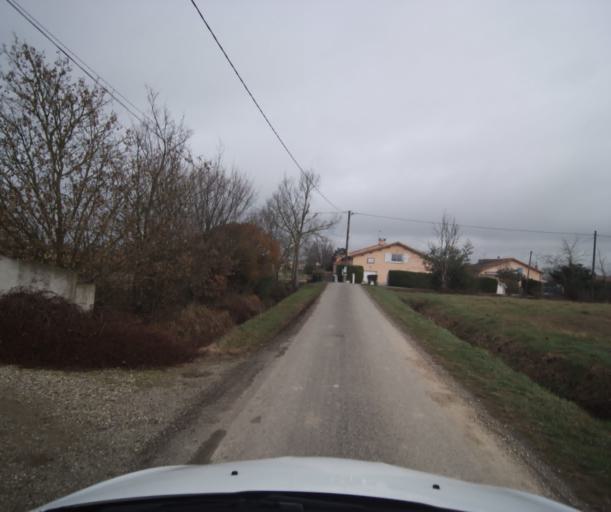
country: FR
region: Midi-Pyrenees
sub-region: Departement du Tarn-et-Garonne
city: Saint-Porquier
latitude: 44.0271
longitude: 1.1554
